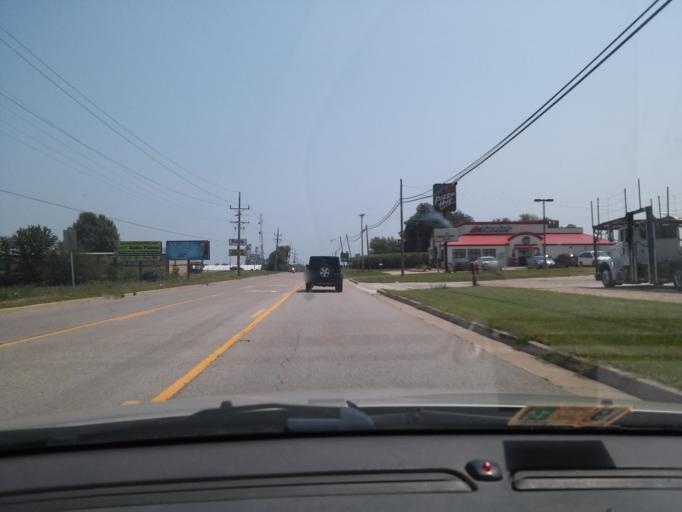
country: US
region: Illinois
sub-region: Pike County
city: Pittsfield
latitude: 39.6046
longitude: -90.8388
